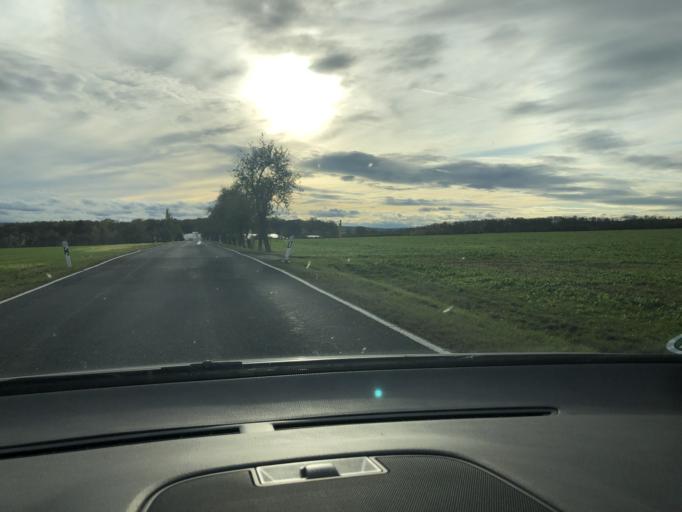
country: DE
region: Thuringia
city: Lehesten
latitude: 50.9642
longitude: 11.5771
